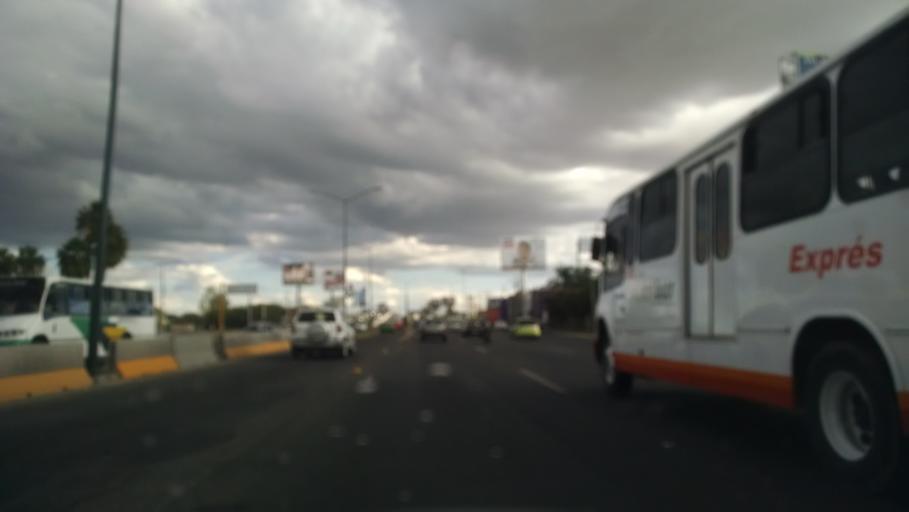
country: MX
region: Guanajuato
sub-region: Leon
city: Fraccionamiento Paraiso Real
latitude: 21.0932
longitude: -101.6245
